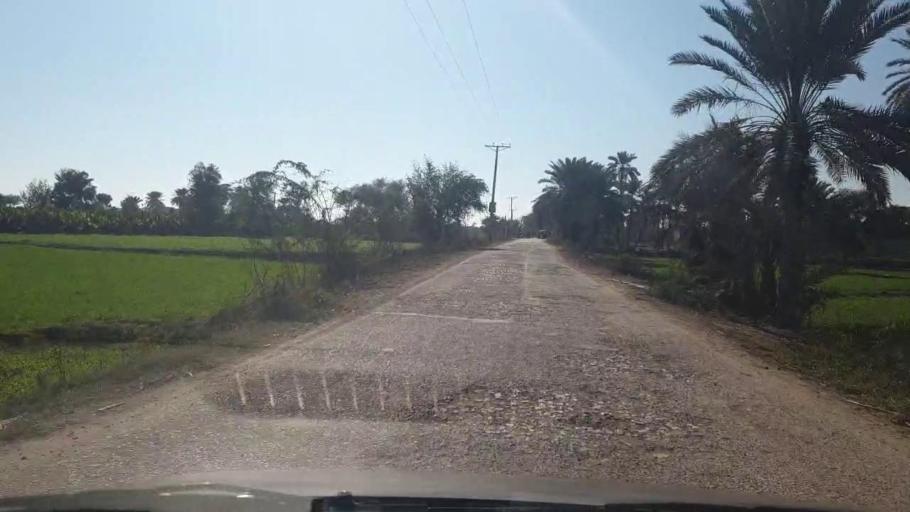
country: PK
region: Sindh
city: Kot Diji
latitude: 27.2759
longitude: 68.6512
